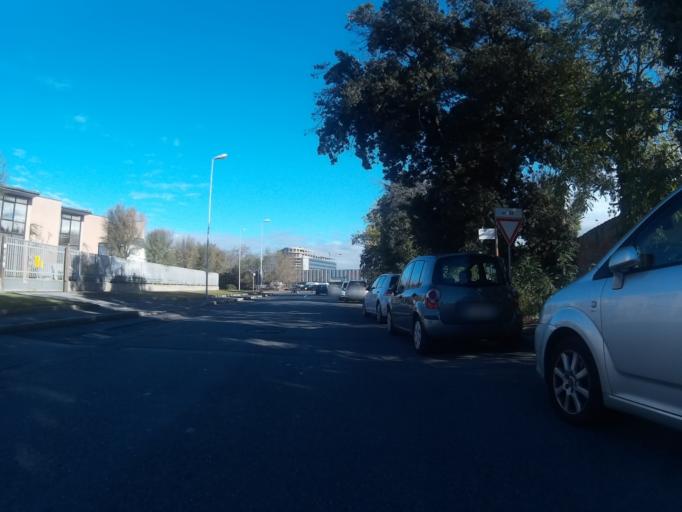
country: IT
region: Tuscany
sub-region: Provincia di Livorno
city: Livorno
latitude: 43.5677
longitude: 10.3400
